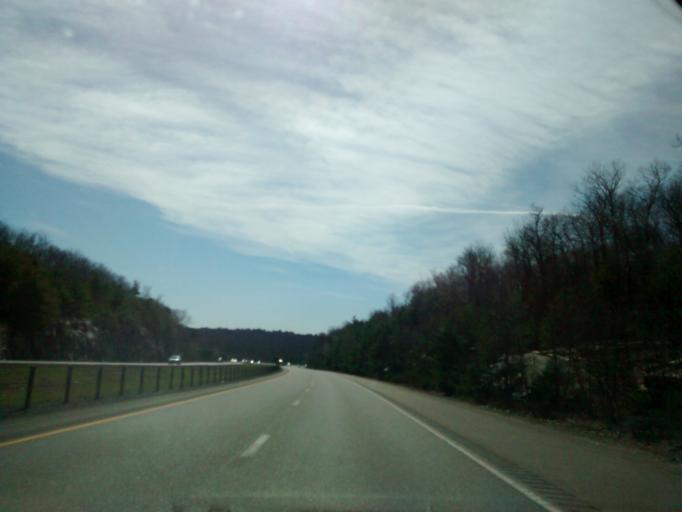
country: US
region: Massachusetts
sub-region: Worcester County
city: Whitinsville
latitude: 42.1389
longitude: -71.7106
